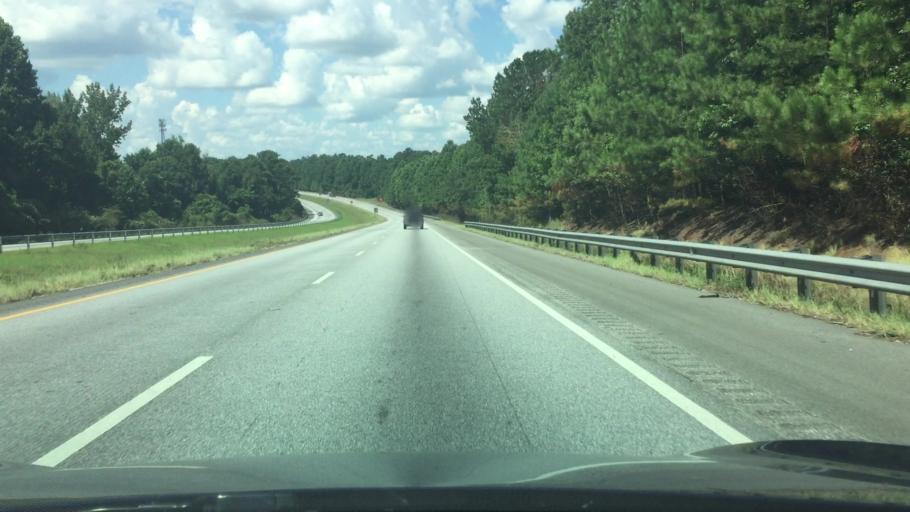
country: US
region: Alabama
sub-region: Lee County
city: Auburn
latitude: 32.5971
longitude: -85.4469
